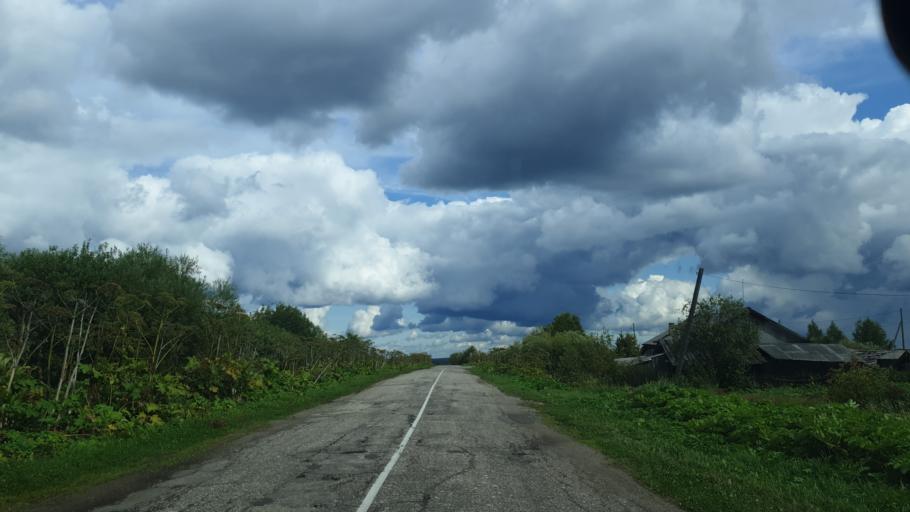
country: RU
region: Komi Republic
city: Aykino
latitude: 61.9561
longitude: 50.1819
